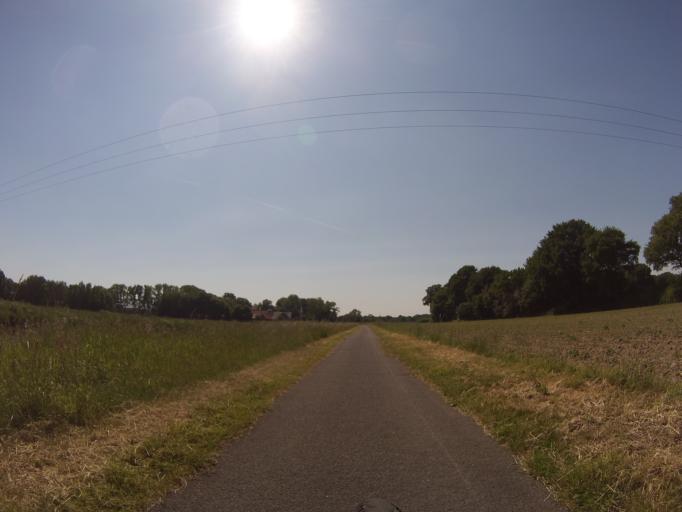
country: DE
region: Lower Saxony
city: Emlichheim
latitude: 52.5984
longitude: 6.8151
